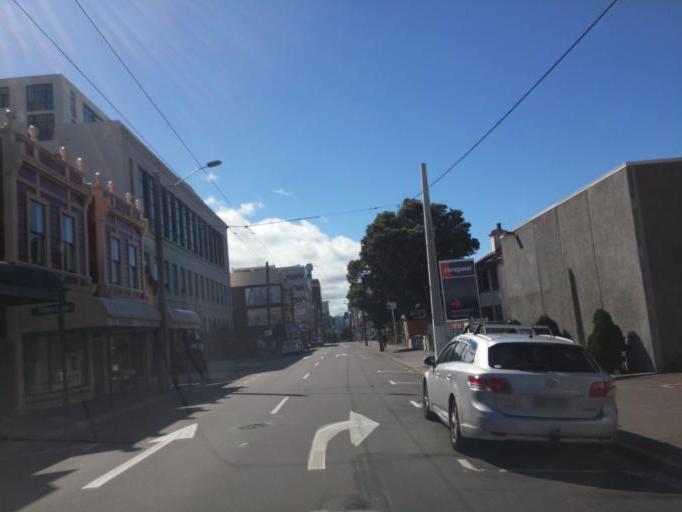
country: NZ
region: Wellington
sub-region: Wellington City
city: Wellington
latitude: -41.2950
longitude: 174.7714
